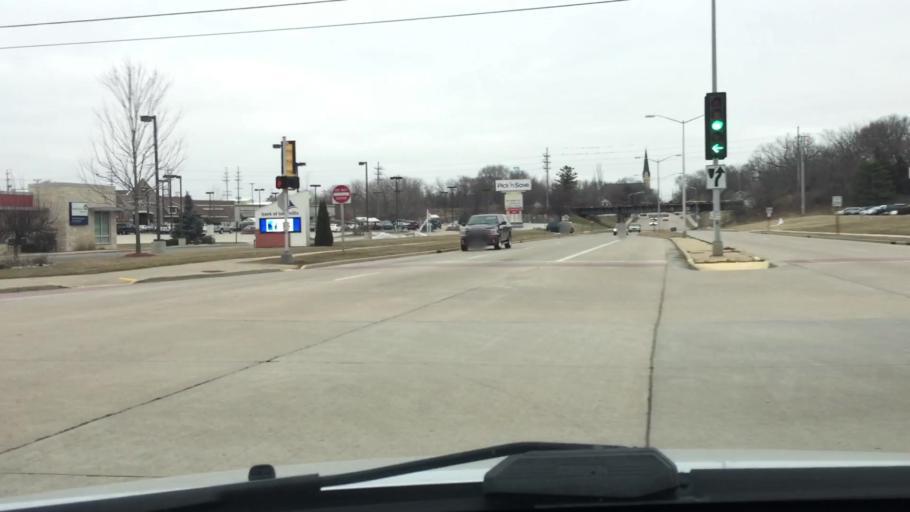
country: US
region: Wisconsin
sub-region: Jefferson County
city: Watertown
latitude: 43.1864
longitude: -88.7301
